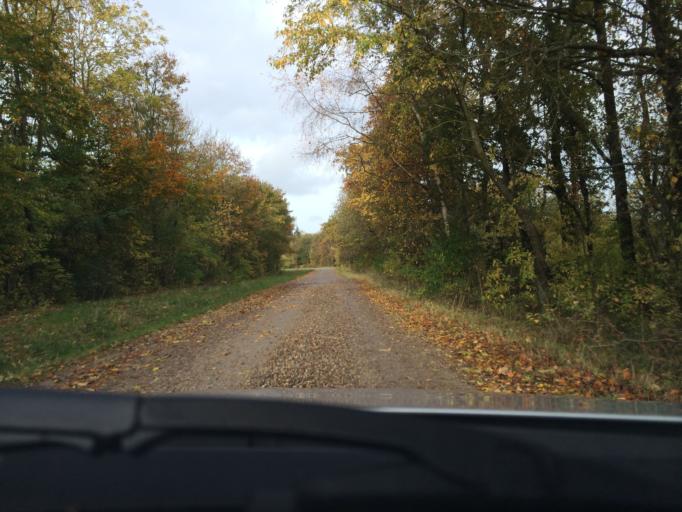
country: DK
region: Central Jutland
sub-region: Holstebro Kommune
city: Ulfborg
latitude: 56.2898
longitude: 8.3834
